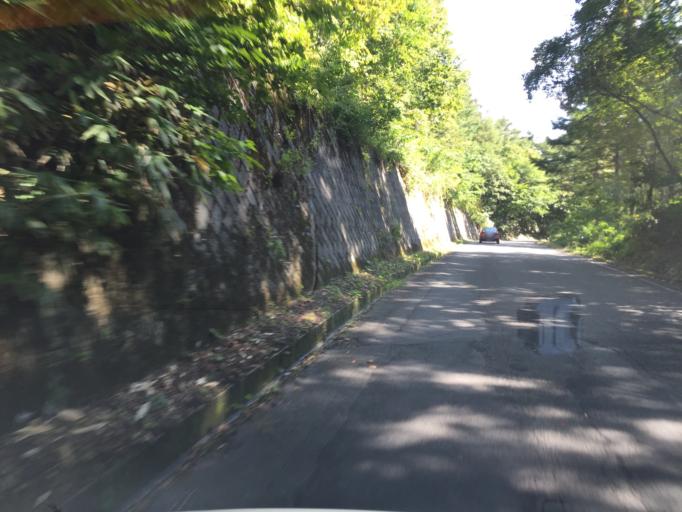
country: JP
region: Fukushima
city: Inawashiro
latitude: 37.6493
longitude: 140.2151
